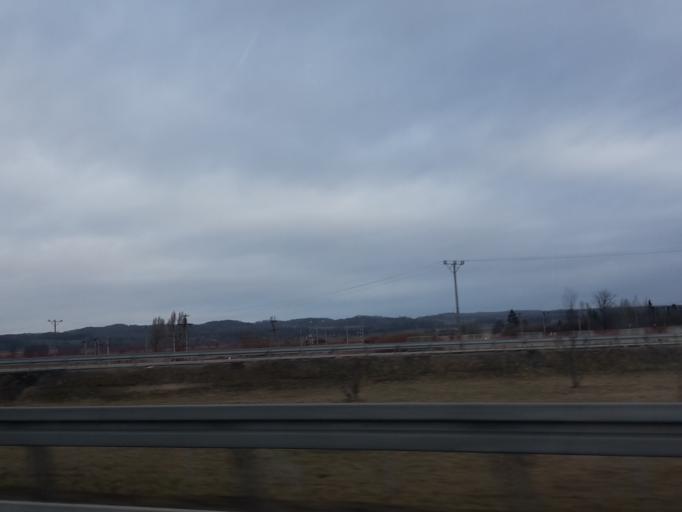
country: PL
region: Warmian-Masurian Voivodeship
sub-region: Powiat elblaski
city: Paslek
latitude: 54.0964
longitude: 19.5631
